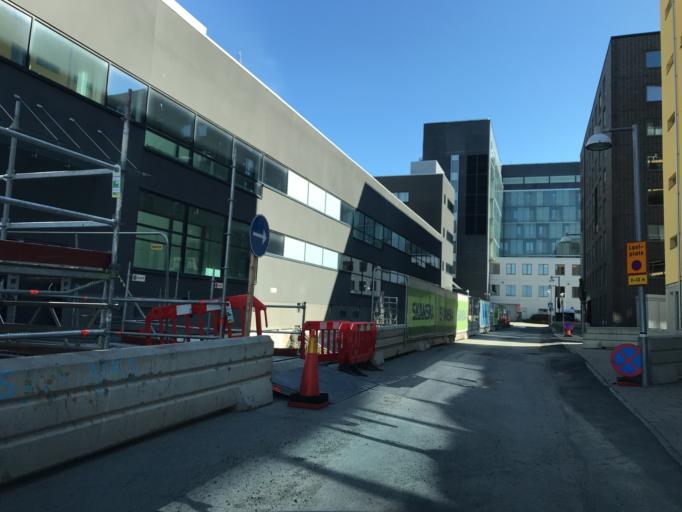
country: SE
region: Stockholm
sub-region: Sollentuna Kommun
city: Sollentuna
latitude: 59.4279
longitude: 17.9471
